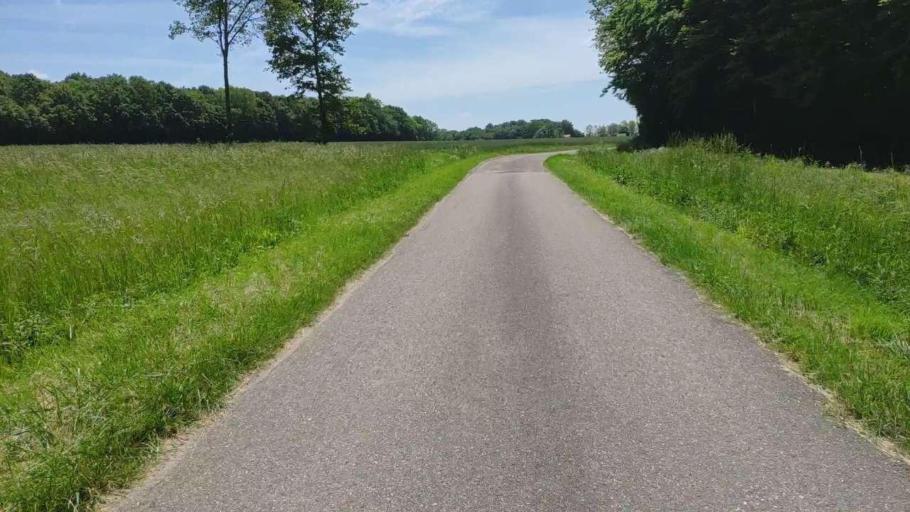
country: FR
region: Franche-Comte
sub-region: Departement du Jura
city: Bletterans
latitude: 46.7753
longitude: 5.3747
